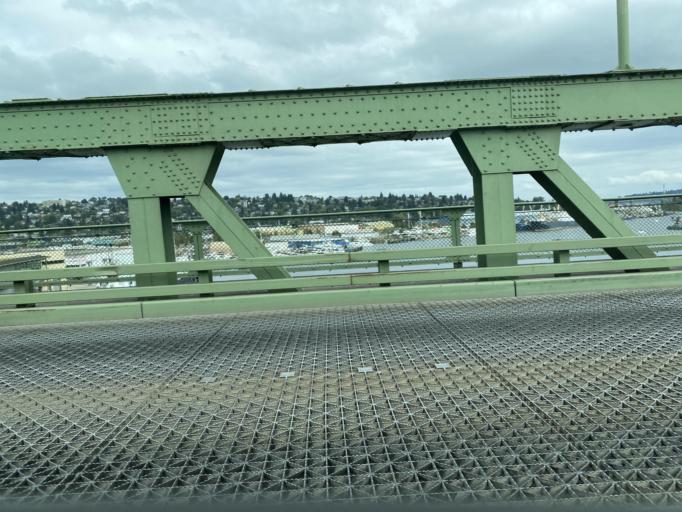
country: US
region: Washington
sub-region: King County
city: Seattle
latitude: 47.6598
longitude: -122.3777
